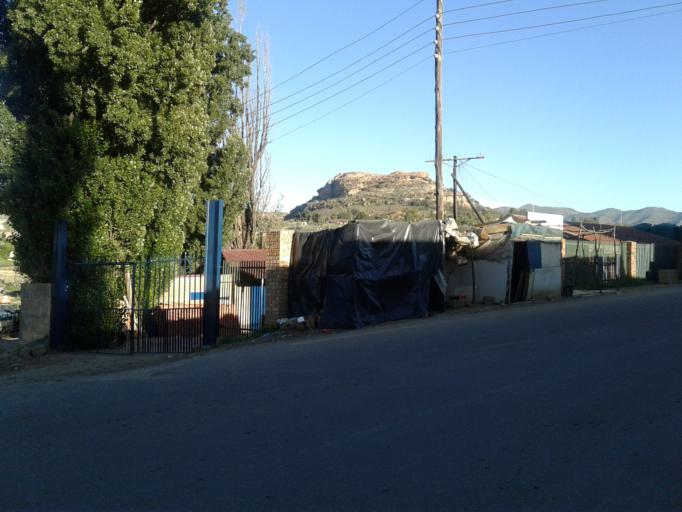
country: LS
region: Butha-Buthe
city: Butha-Buthe
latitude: -28.7648
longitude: 28.2514
